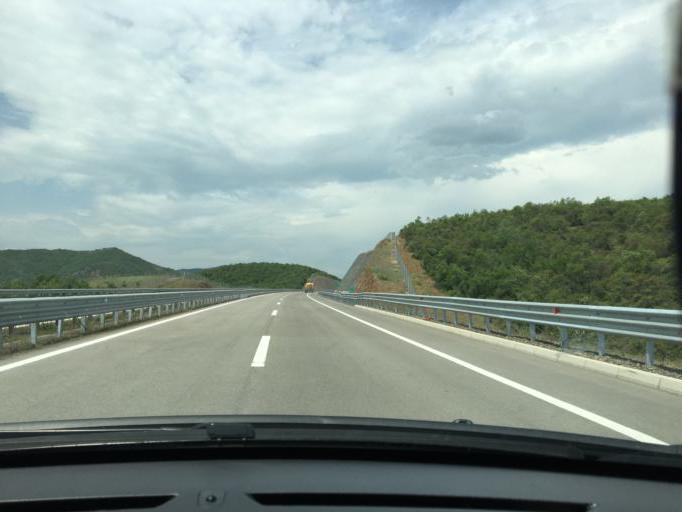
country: MK
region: Gevgelija
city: Miravci
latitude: 41.3158
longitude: 22.4120
